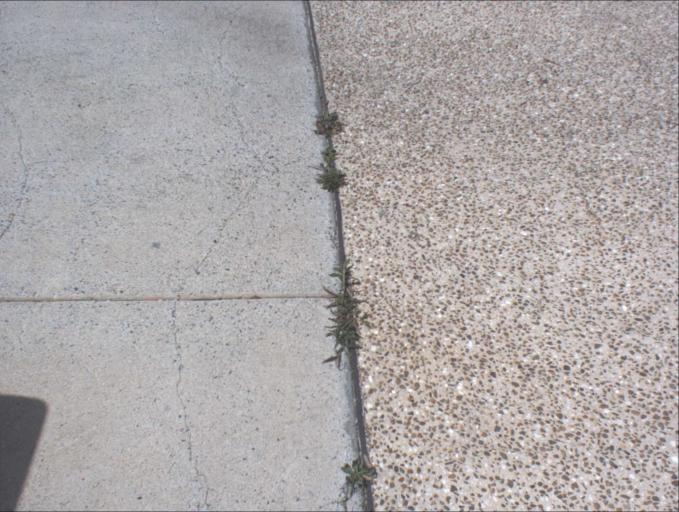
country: AU
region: Queensland
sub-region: Logan
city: Chambers Flat
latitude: -27.7983
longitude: 153.1099
